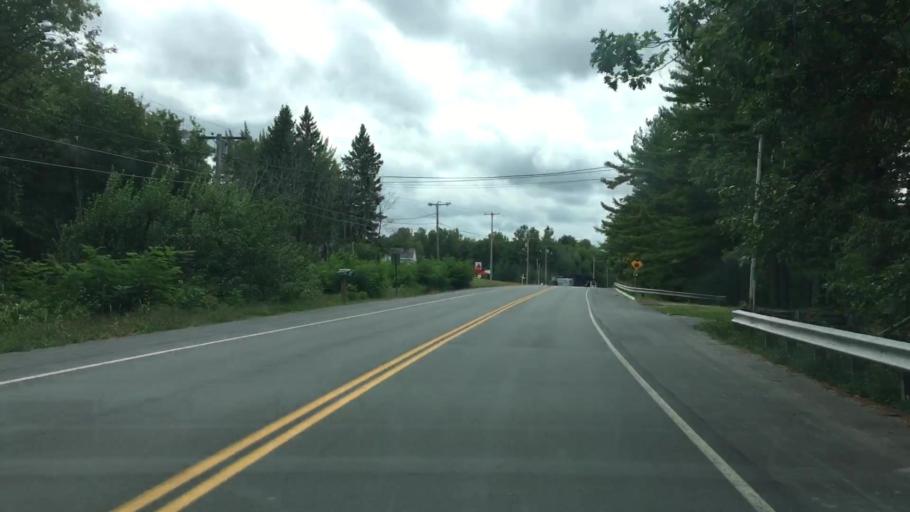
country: US
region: Maine
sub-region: Penobscot County
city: Milford
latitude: 44.9548
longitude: -68.6981
